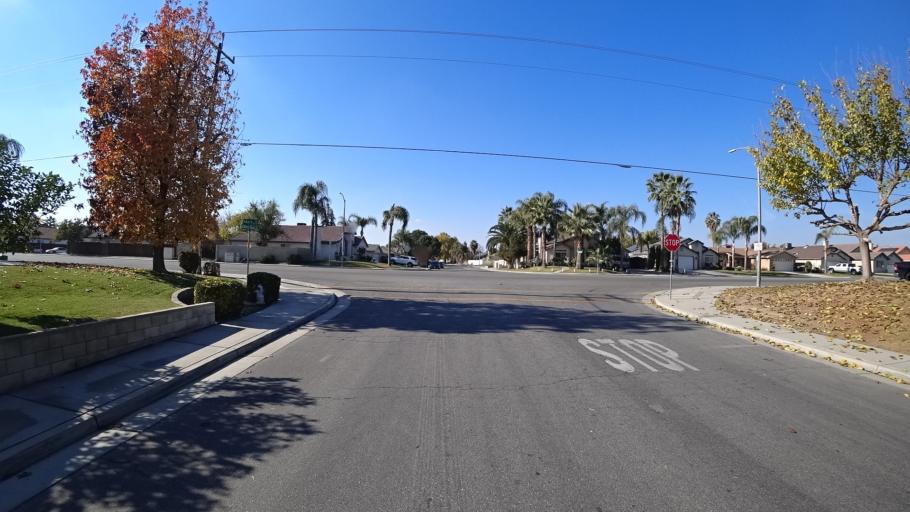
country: US
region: California
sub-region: Kern County
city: Greenfield
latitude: 35.2909
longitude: -119.0475
